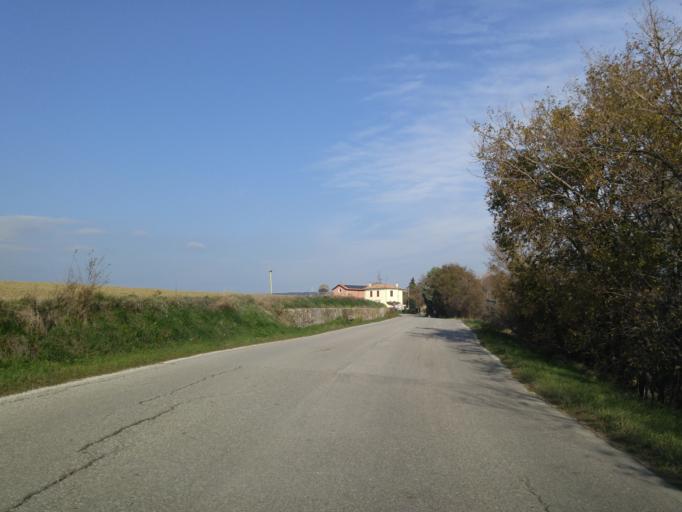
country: IT
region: The Marches
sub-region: Provincia di Pesaro e Urbino
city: Lucrezia
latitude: 43.8000
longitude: 12.9131
